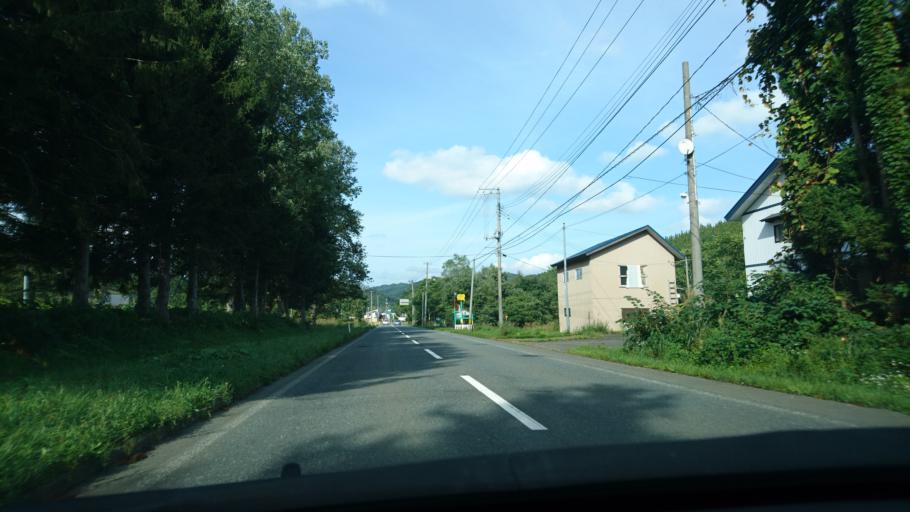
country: JP
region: Akita
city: Yokotemachi
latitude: 39.3075
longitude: 140.7450
